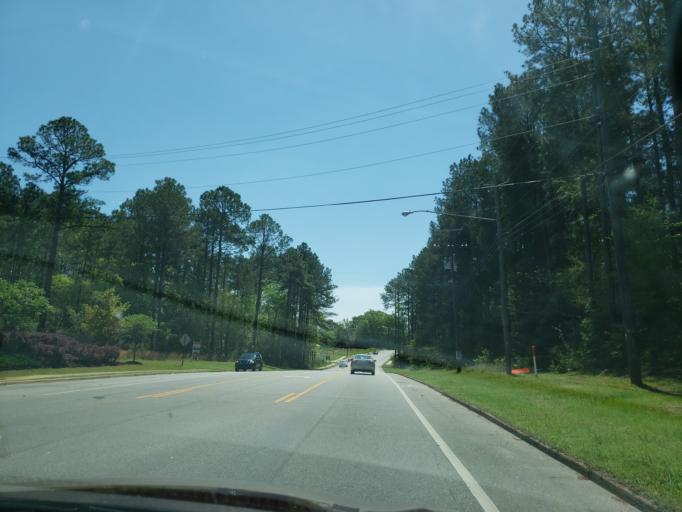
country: US
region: Alabama
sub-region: Lee County
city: Auburn
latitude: 32.6291
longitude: -85.4965
